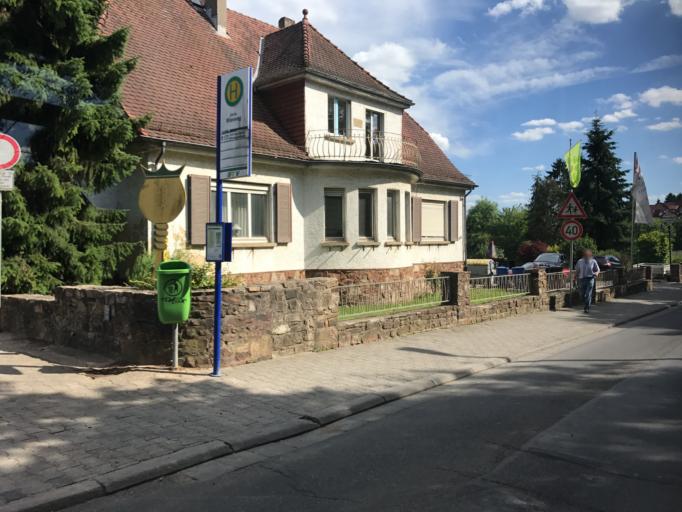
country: DE
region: Hesse
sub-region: Regierungsbezirk Darmstadt
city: Eltville
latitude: 50.0376
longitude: 8.1174
